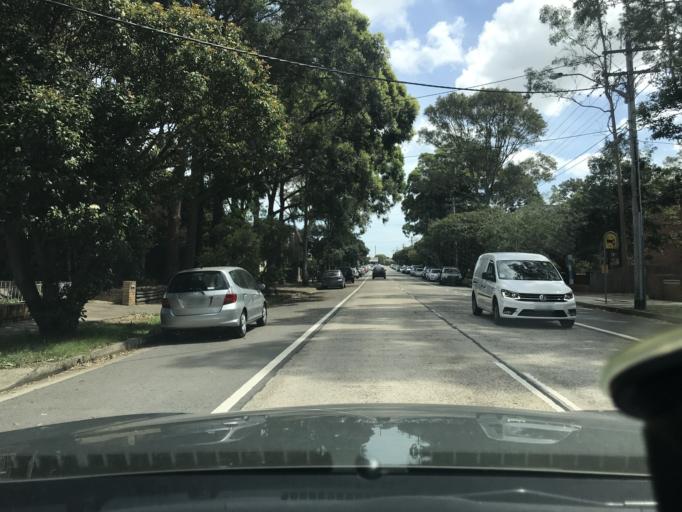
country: AU
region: New South Wales
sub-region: Canada Bay
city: Wareemba
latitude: -33.8551
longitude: 151.1339
